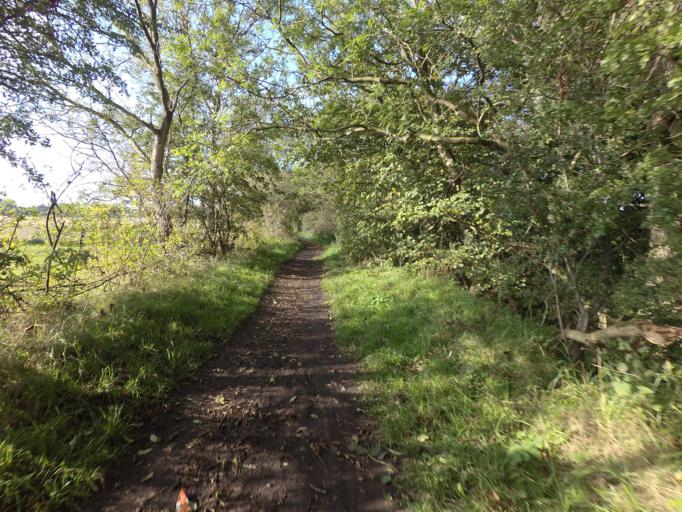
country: GB
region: Scotland
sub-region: West Lothian
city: East Calder
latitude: 55.9034
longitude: -3.4674
